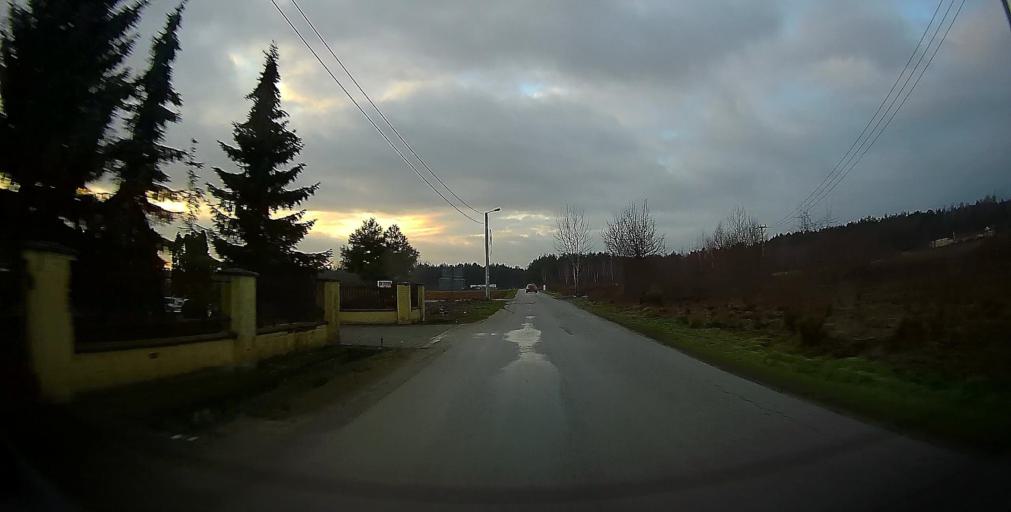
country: PL
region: Masovian Voivodeship
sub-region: Powiat radomski
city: Jedlinsk
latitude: 51.4587
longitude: 21.1082
